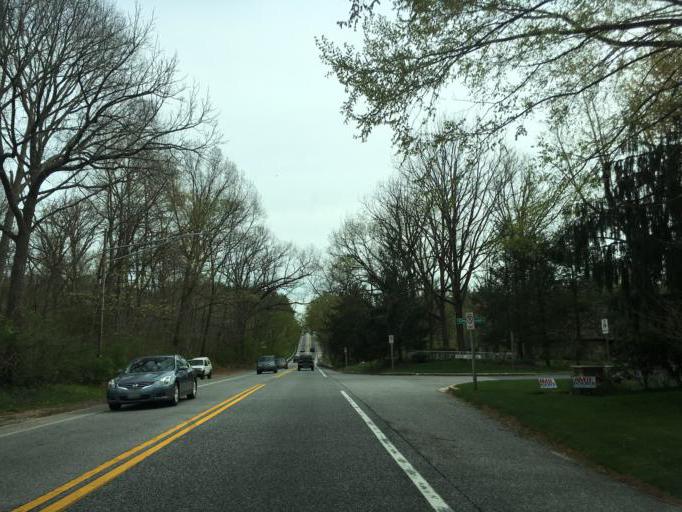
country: US
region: Maryland
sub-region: Baltimore County
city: Hampton
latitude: 39.4415
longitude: -76.5969
